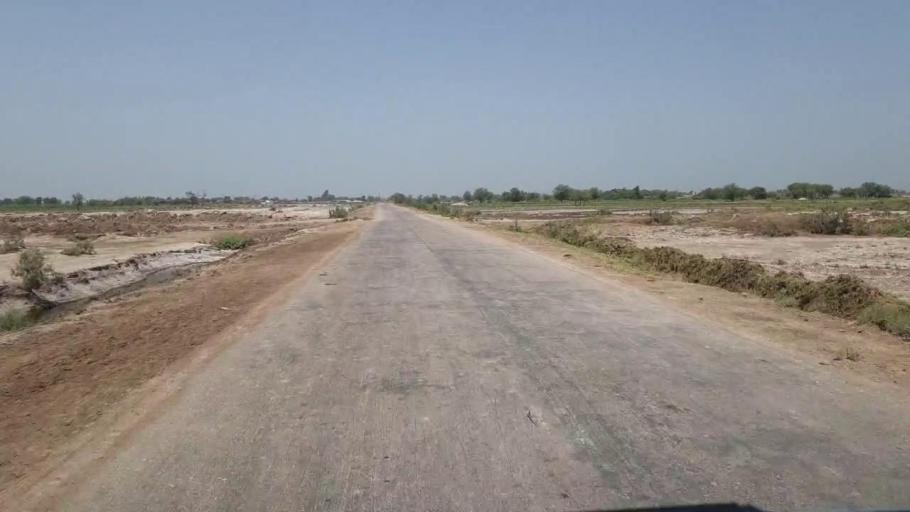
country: PK
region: Sindh
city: Nawabshah
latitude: 26.3609
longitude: 68.4053
